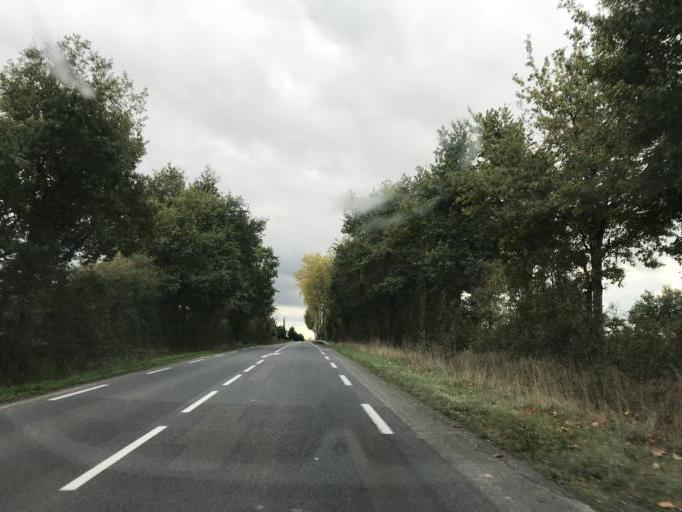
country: FR
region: Rhone-Alpes
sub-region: Departement de l'Ain
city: Chatillon-sur-Chalaronne
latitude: 46.1008
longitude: 4.9325
